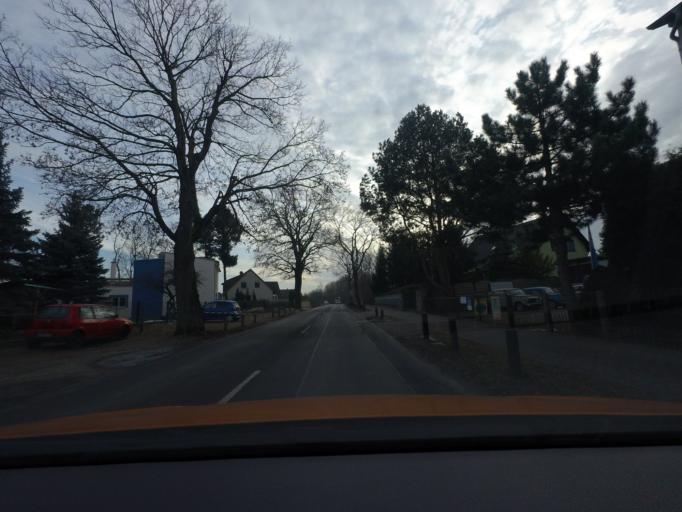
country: DE
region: Berlin
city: Blankenfelde
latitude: 52.6599
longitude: 13.3766
